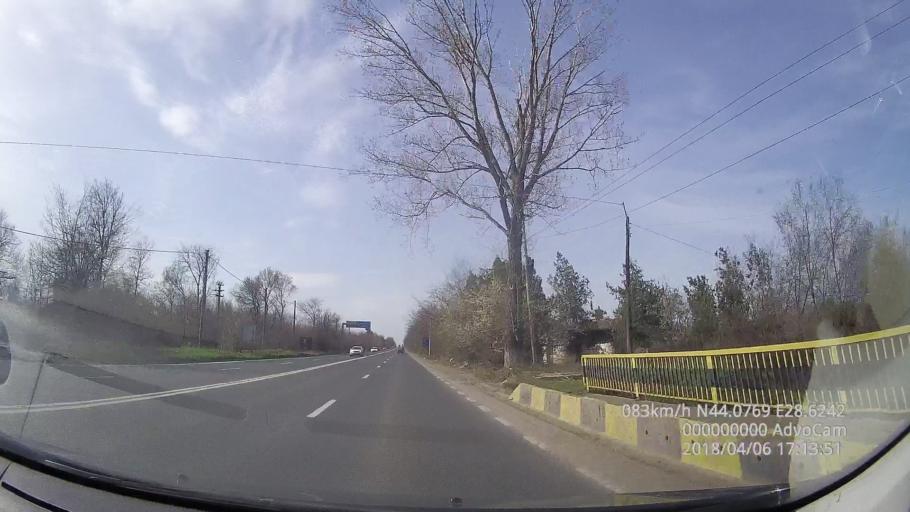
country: RO
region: Constanta
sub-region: Comuna Agigea
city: Agigea
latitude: 44.0775
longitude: 28.6236
